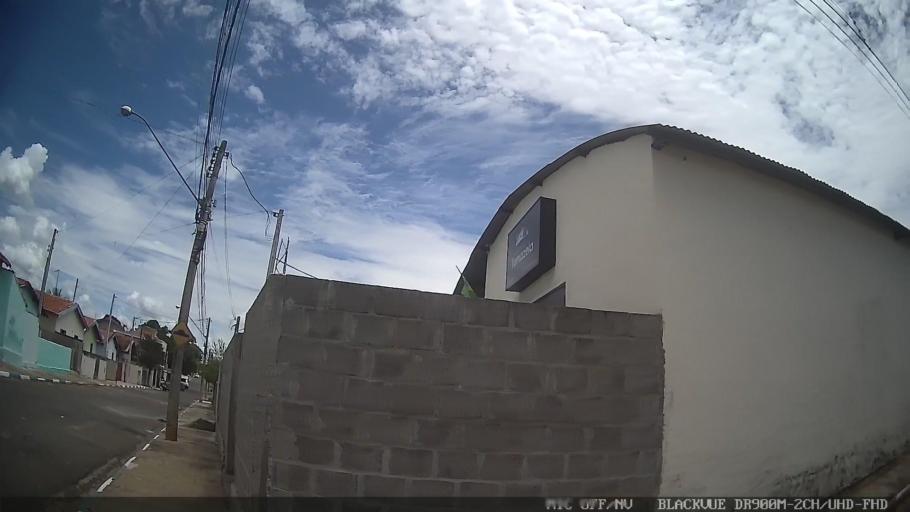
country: BR
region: Sao Paulo
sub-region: Conchas
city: Conchas
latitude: -23.0706
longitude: -47.9775
